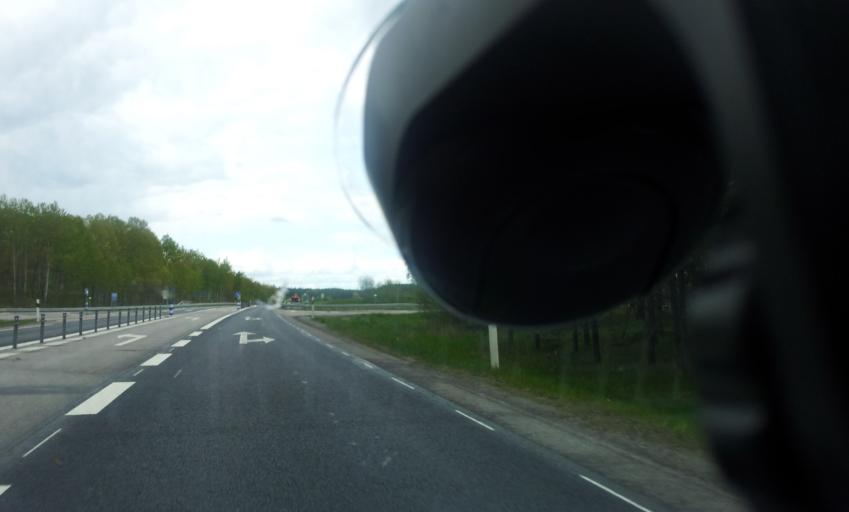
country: SE
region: OEstergoetland
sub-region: Soderkopings Kommun
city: Soederkoeping
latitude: 58.5081
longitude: 16.2934
